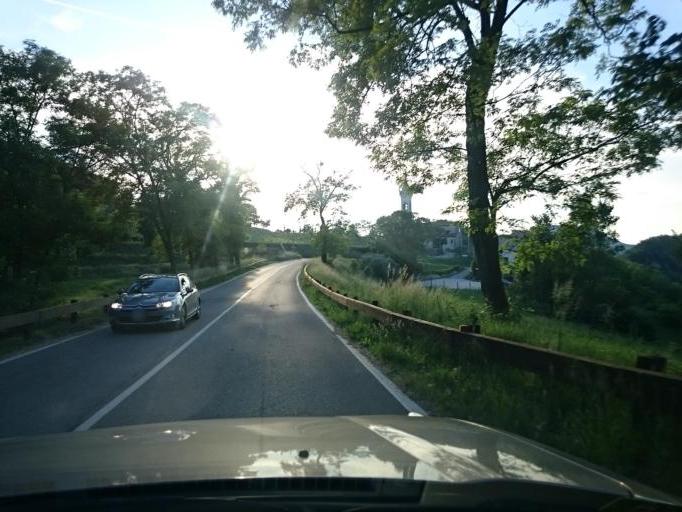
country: IT
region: Veneto
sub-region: Provincia di Padova
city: Treponti
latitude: 45.3297
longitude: 11.6894
